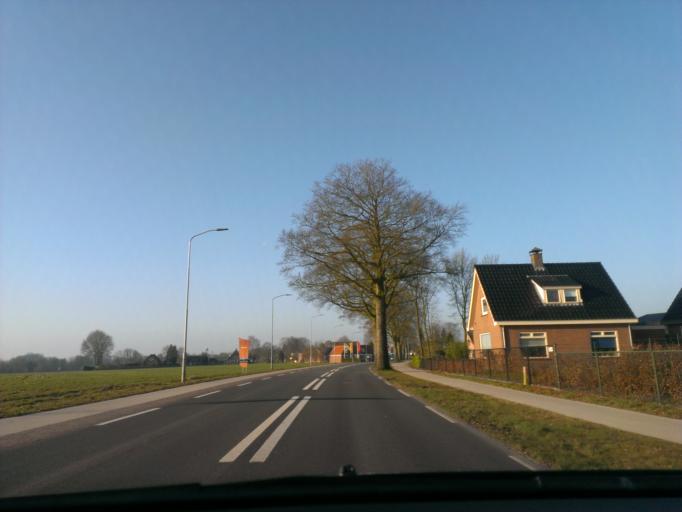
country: NL
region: Gelderland
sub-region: Gemeente Heerde
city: Heerde
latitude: 52.3796
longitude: 6.0317
